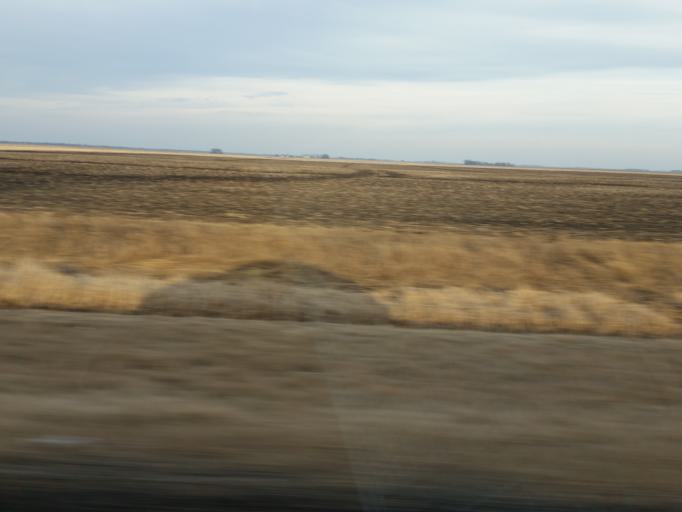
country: US
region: North Dakota
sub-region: Traill County
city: Hillsboro
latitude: 47.2941
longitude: -97.2178
